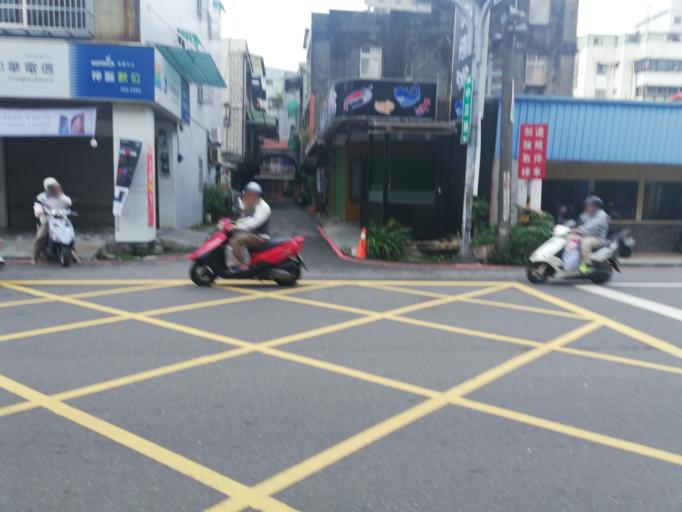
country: TW
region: Taiwan
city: Taoyuan City
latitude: 25.0056
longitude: 121.3042
